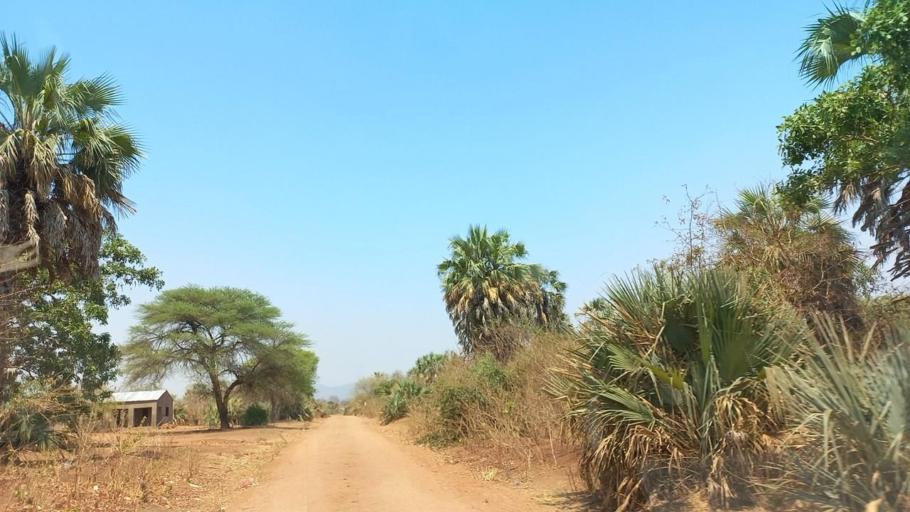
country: ZM
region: Lusaka
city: Luangwa
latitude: -15.1870
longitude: 30.2108
